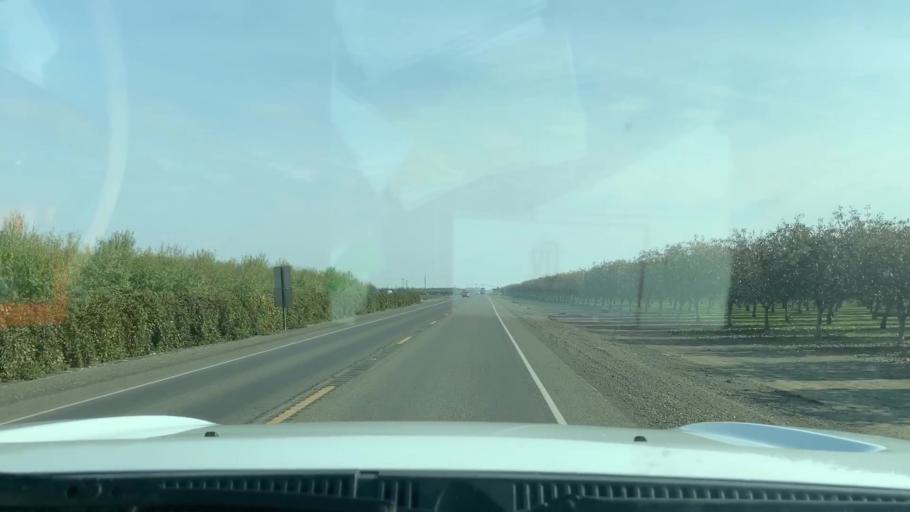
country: US
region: California
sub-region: Fresno County
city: Huron
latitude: 36.2553
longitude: -120.1099
